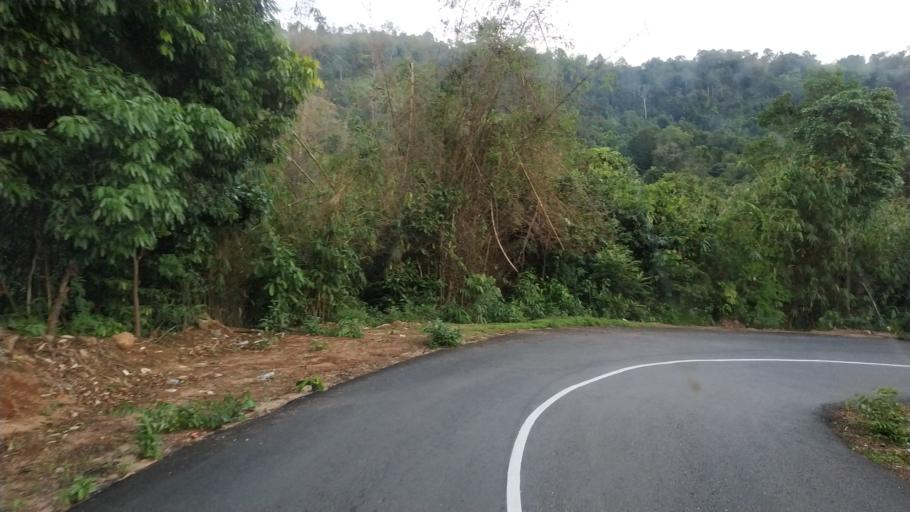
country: MM
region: Mon
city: Kyaikto
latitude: 17.4352
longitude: 97.0956
